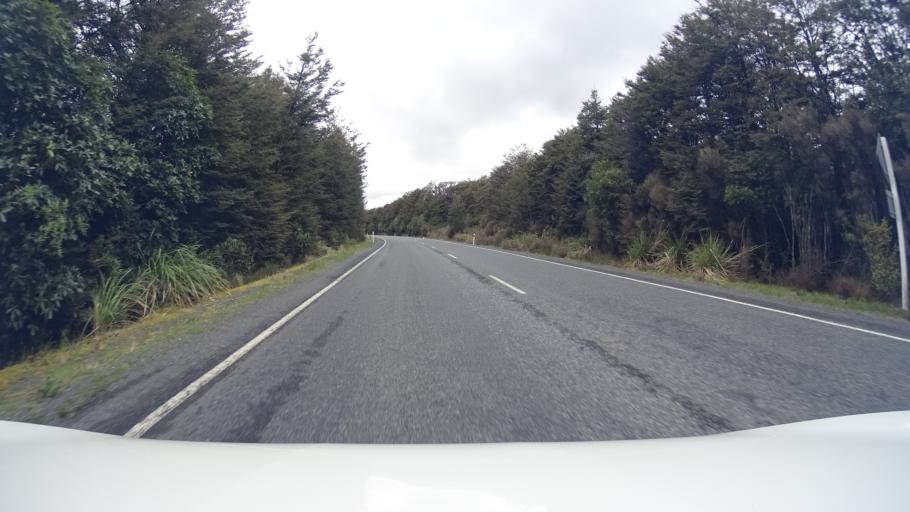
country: NZ
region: Manawatu-Wanganui
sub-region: Ruapehu District
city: Waiouru
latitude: -39.1784
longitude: 175.5173
